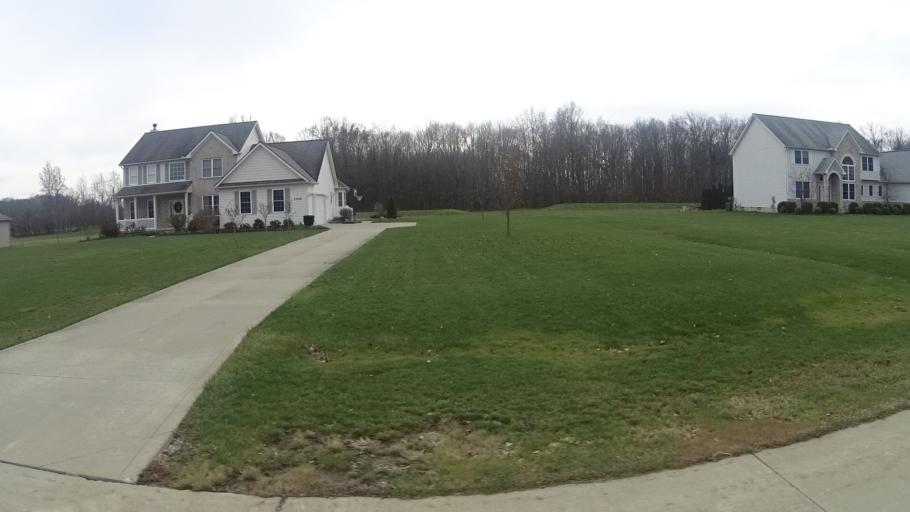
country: US
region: Ohio
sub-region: Lorain County
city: Eaton Estates
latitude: 41.2799
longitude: -81.9593
